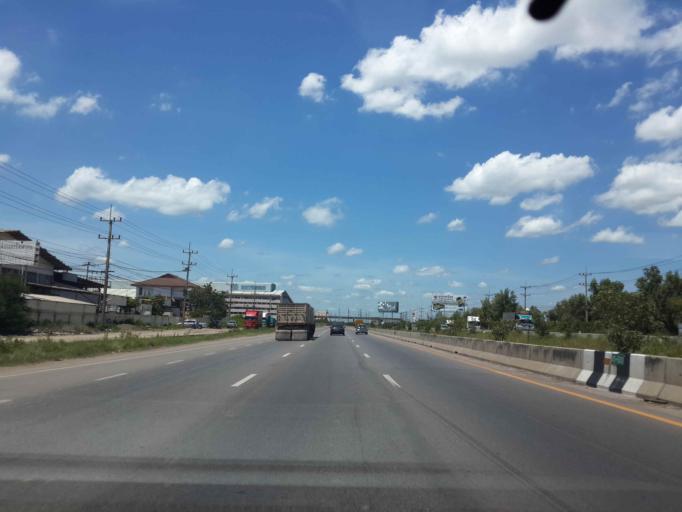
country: TH
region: Samut Sakhon
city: Ban Phaeo
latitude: 13.4991
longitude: 100.1251
